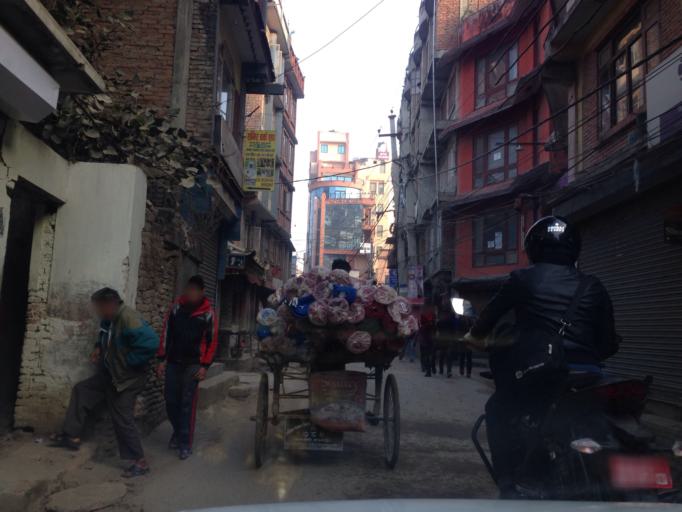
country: NP
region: Central Region
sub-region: Bagmati Zone
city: Kathmandu
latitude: 27.7149
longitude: 85.3085
